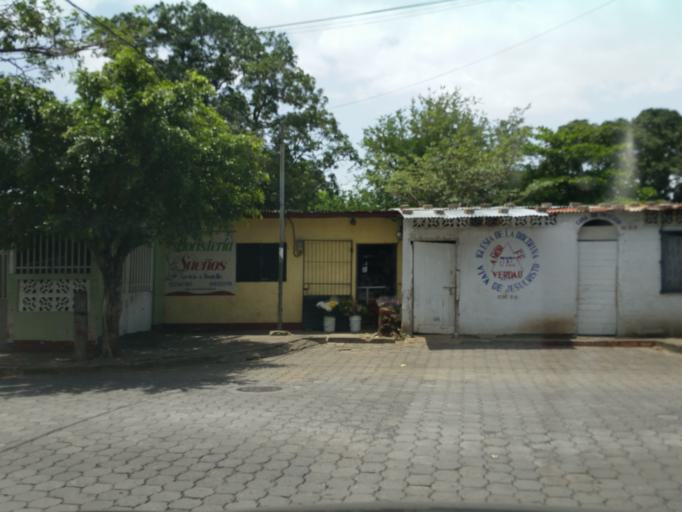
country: NI
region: Managua
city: Managua
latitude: 12.1402
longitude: -86.2469
